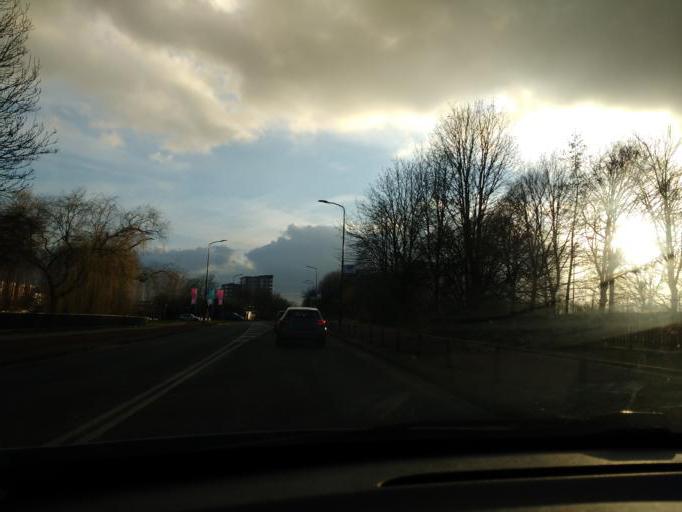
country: NL
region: Utrecht
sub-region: Gemeente Veenendaal
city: Veenendaal
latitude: 52.0288
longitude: 5.5424
